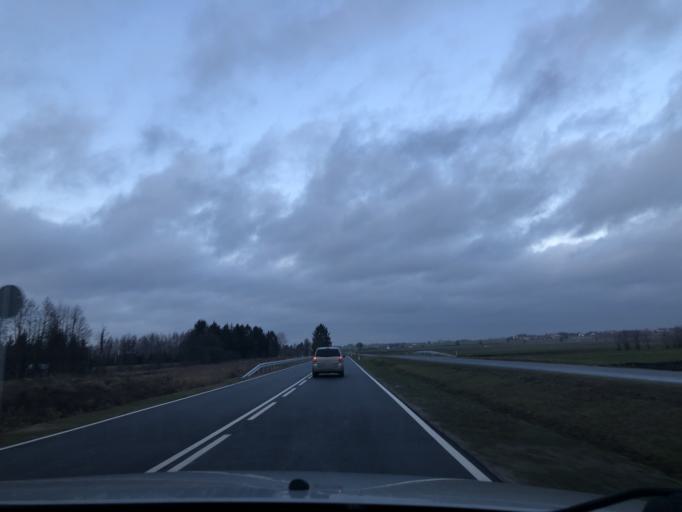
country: PL
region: Podlasie
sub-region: Lomza
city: Lomza
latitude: 53.1293
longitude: 22.0484
